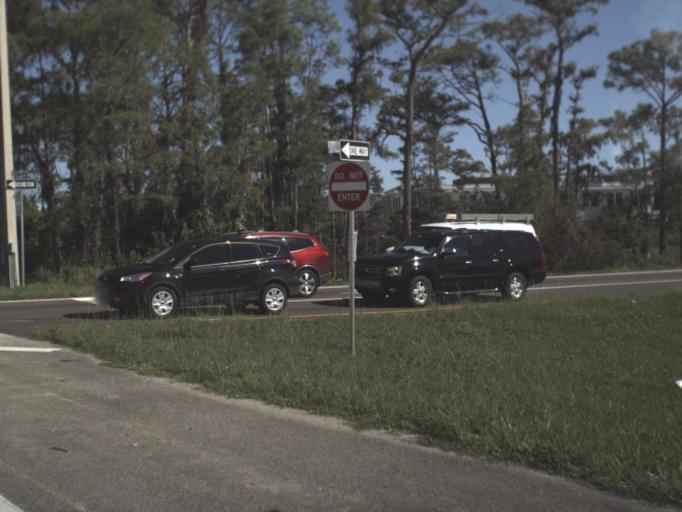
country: US
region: Florida
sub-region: Lee County
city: Gateway
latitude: 26.5472
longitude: -81.7932
